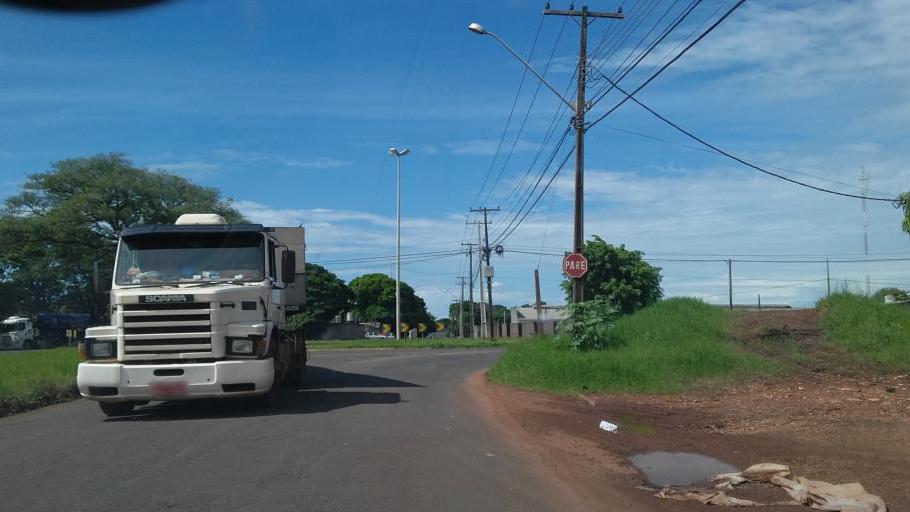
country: BR
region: Parana
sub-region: Londrina
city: Londrina
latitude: -23.2851
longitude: -51.2099
